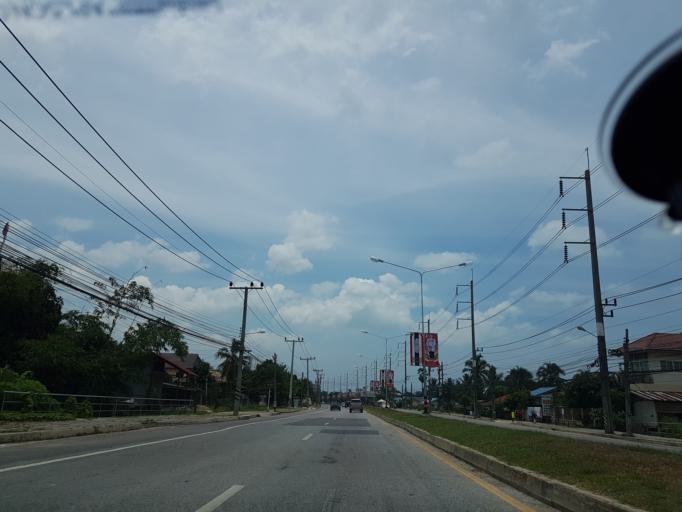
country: TH
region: Songkhla
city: Songkhla
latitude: 7.1096
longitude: 100.6328
